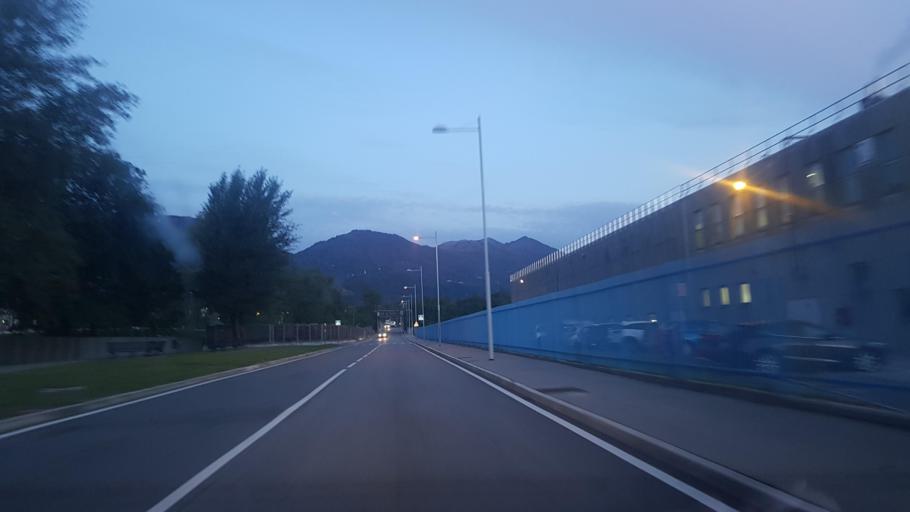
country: IT
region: Friuli Venezia Giulia
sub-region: Provincia di Udine
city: Tolmezzo
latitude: 46.3909
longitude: 13.0255
